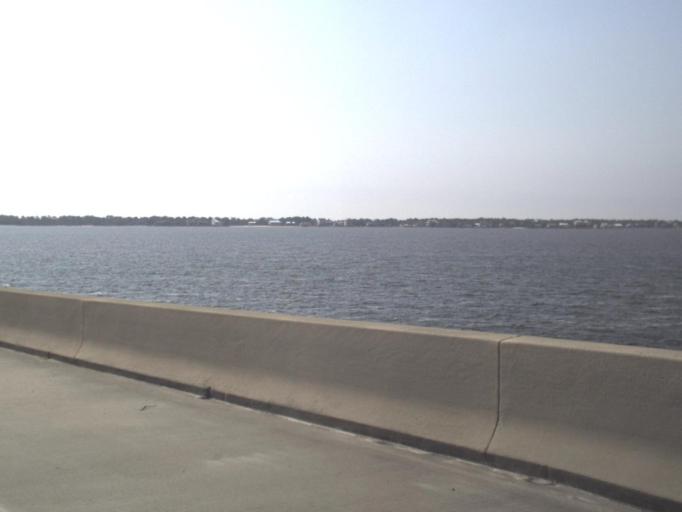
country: US
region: Florida
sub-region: Franklin County
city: Eastpoint
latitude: 29.6794
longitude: -84.8759
